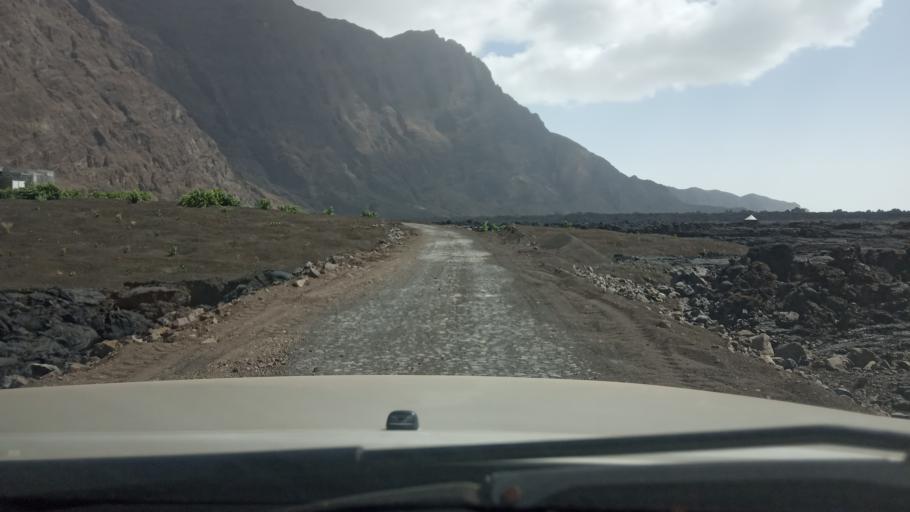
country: CV
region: Santa Catarina do Fogo
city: Cova Figueira
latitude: 14.9406
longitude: -24.3843
